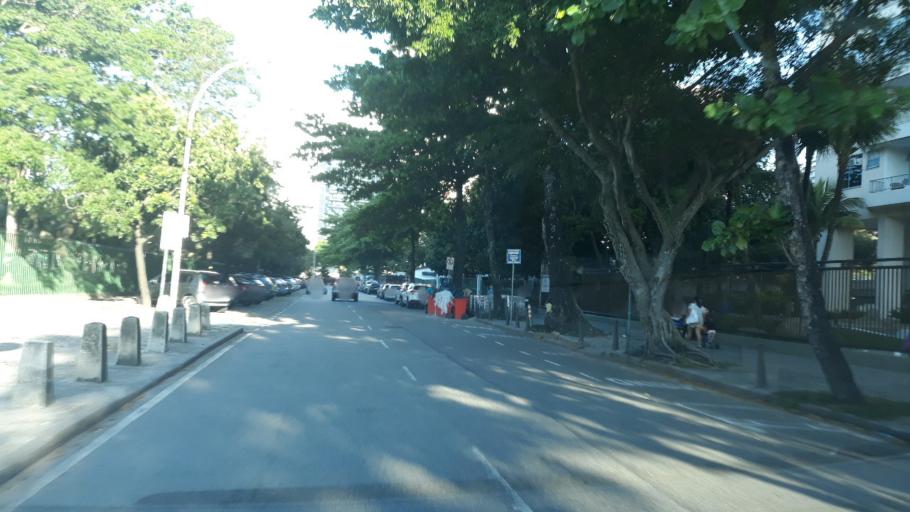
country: BR
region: Rio de Janeiro
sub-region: Rio De Janeiro
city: Rio de Janeiro
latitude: -23.0023
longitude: -43.3516
